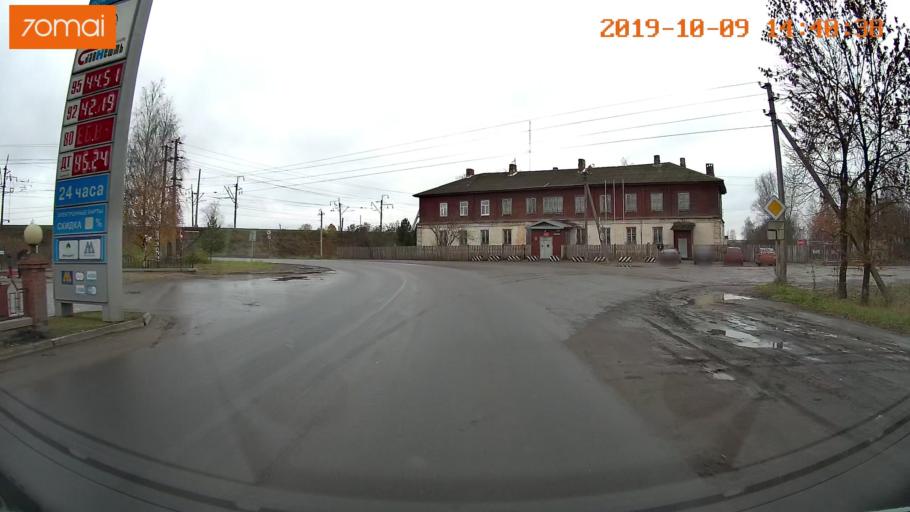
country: RU
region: Kostroma
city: Buy
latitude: 58.4749
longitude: 41.5300
